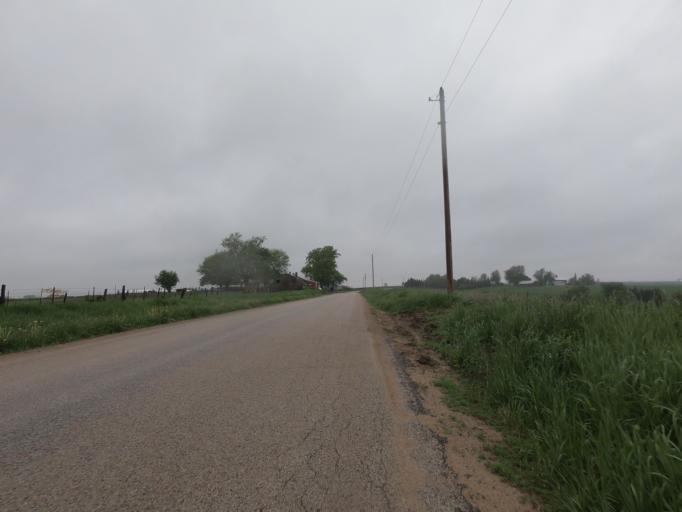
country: US
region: Wisconsin
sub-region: Grant County
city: Hazel Green
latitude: 42.4971
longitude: -90.5018
